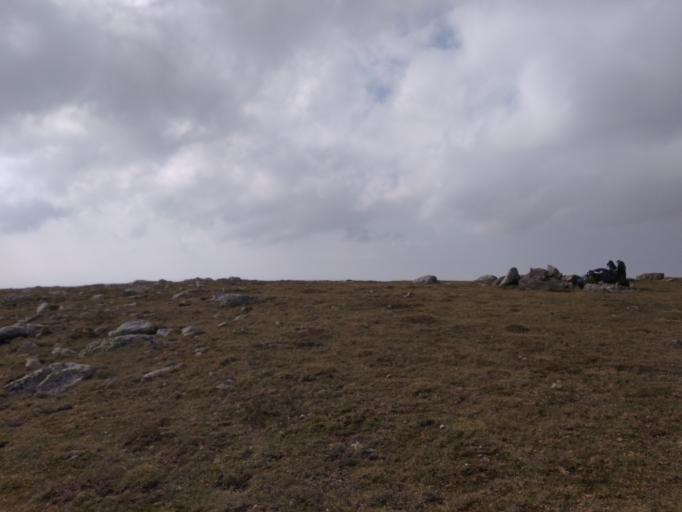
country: BG
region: Plovdiv
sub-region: Obshtina Karlovo
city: Kalofer
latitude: 42.7329
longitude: 24.9673
